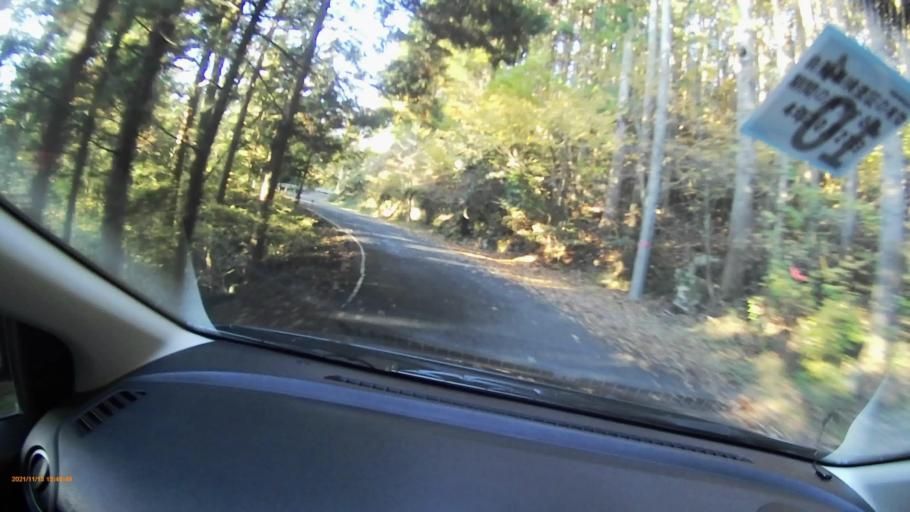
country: JP
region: Gifu
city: Nakatsugawa
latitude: 35.5853
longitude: 137.3889
